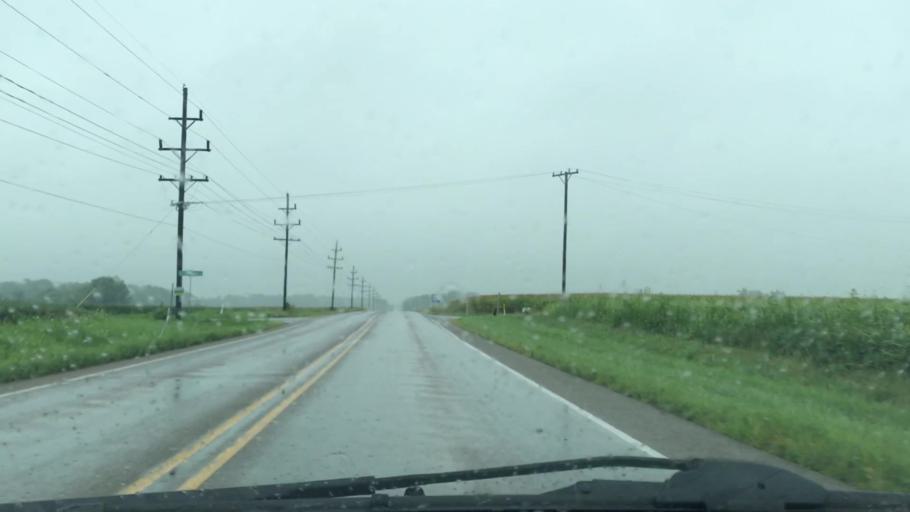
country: US
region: Indiana
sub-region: Hamilton County
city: Sheridan
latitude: 40.1105
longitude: -86.1653
